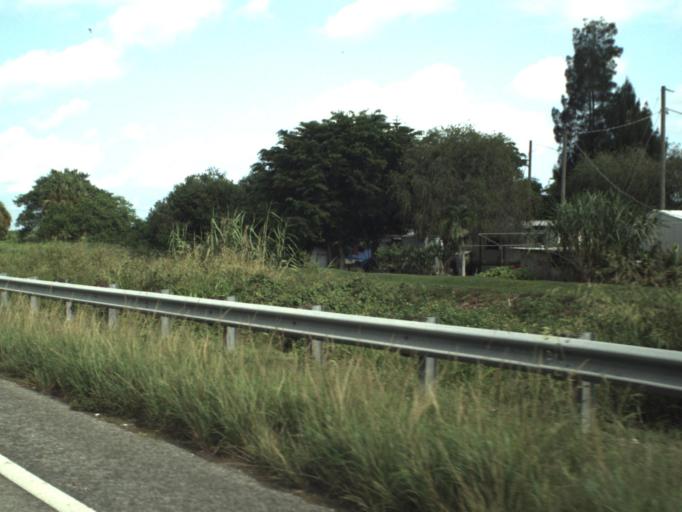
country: US
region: Florida
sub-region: Palm Beach County
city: Belle Glade Camp
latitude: 26.6639
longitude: -80.6840
